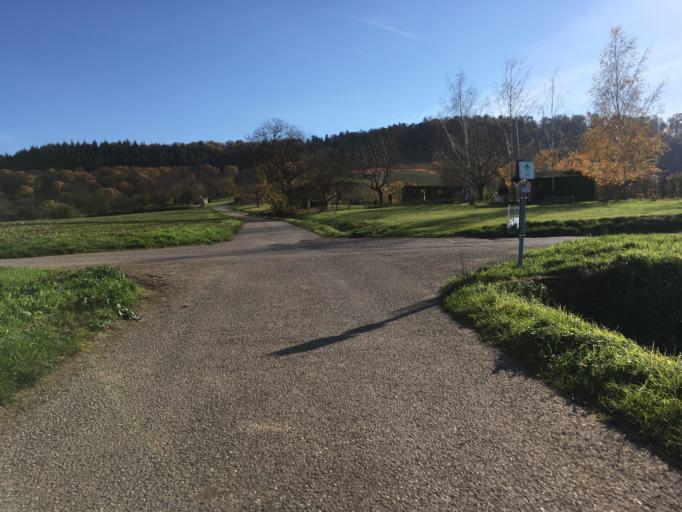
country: DE
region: Baden-Wuerttemberg
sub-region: Karlsruhe Region
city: Oberderdingen
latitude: 49.0534
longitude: 8.8056
